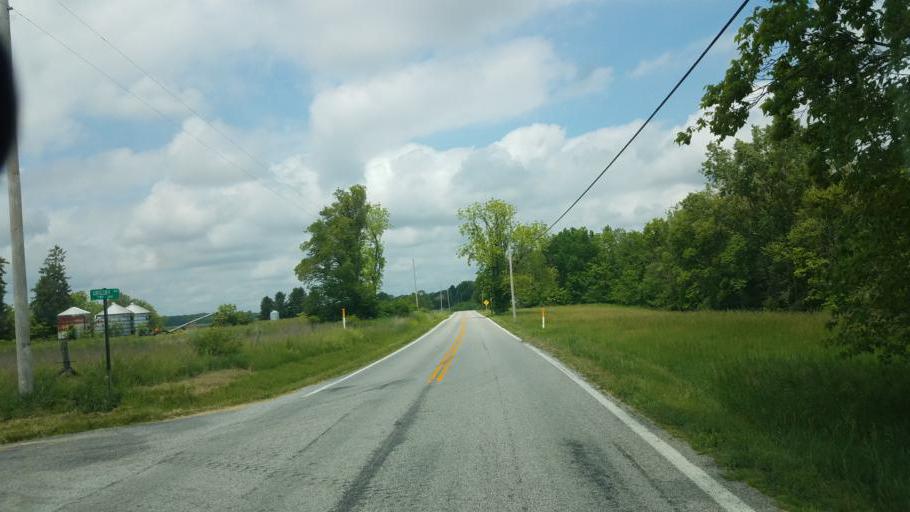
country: US
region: Ohio
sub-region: Marion County
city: Prospect
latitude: 40.4342
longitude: -83.1950
